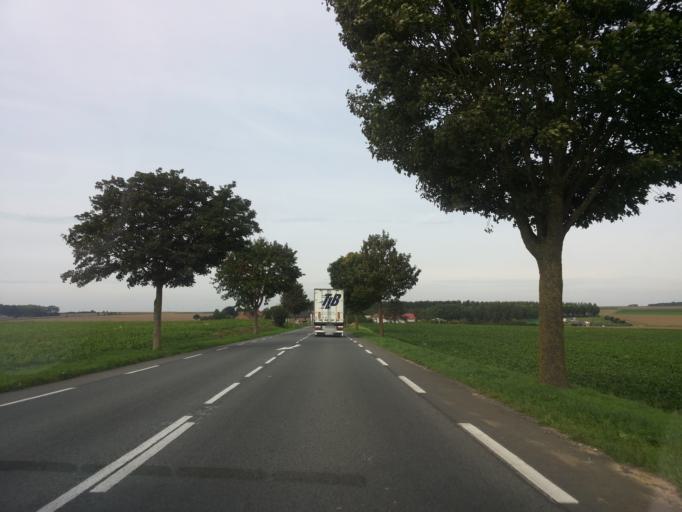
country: FR
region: Nord-Pas-de-Calais
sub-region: Departement du Nord
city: Lecluse
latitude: 50.2265
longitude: 3.0260
